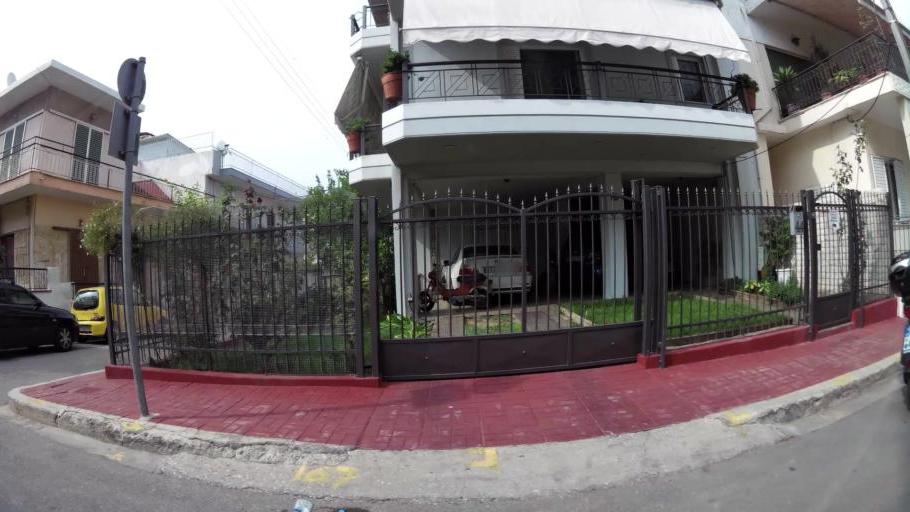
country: GR
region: Attica
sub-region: Nomarchia Athinas
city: Peristeri
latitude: 38.0097
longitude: 23.6847
